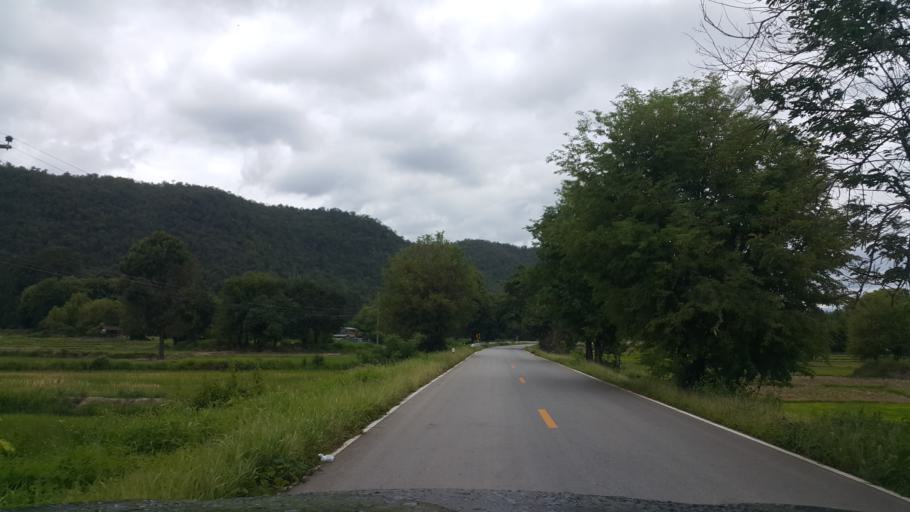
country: TH
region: Phitsanulok
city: Chat Trakan
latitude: 17.3127
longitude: 100.6731
